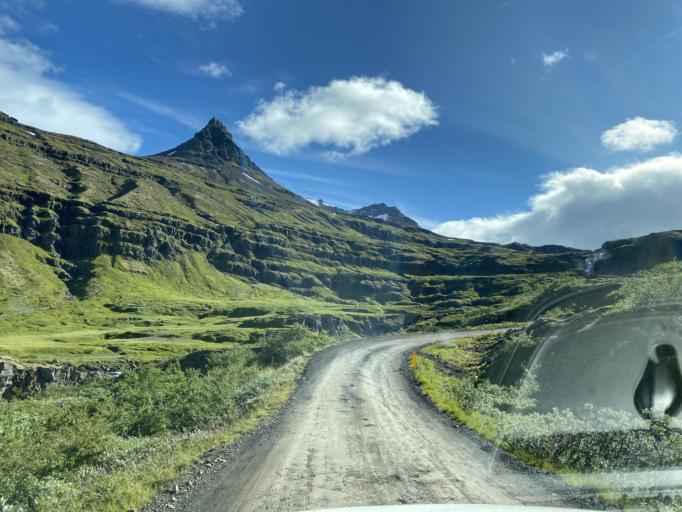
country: IS
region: East
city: Eskifjoerdur
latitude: 65.1825
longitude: -14.0726
